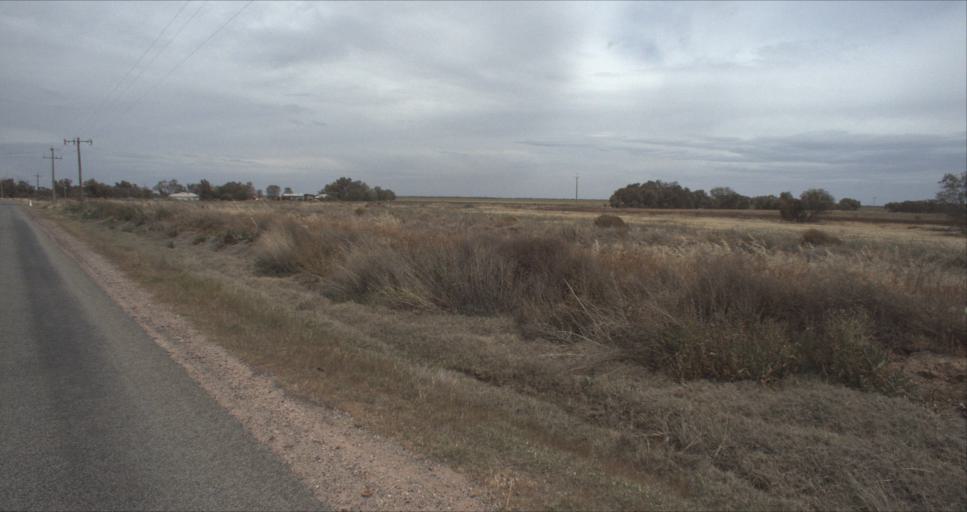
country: AU
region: New South Wales
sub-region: Leeton
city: Leeton
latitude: -34.4390
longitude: 146.3760
